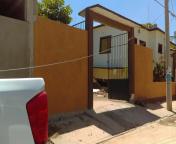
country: MX
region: Oaxaca
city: Asuncion Ixtaltepec
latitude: 16.5038
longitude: -95.0594
